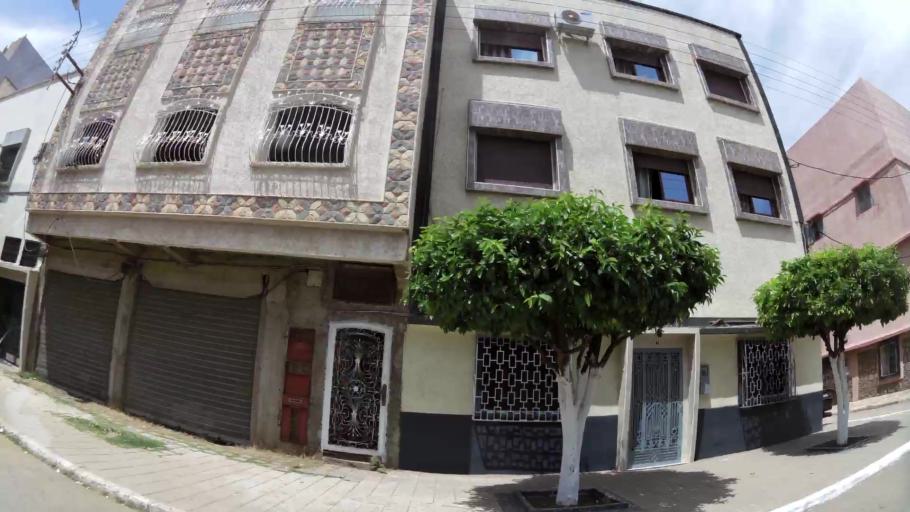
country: MA
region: Rabat-Sale-Zemmour-Zaer
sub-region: Khemisset
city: Khemisset
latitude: 33.8205
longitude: -6.0718
